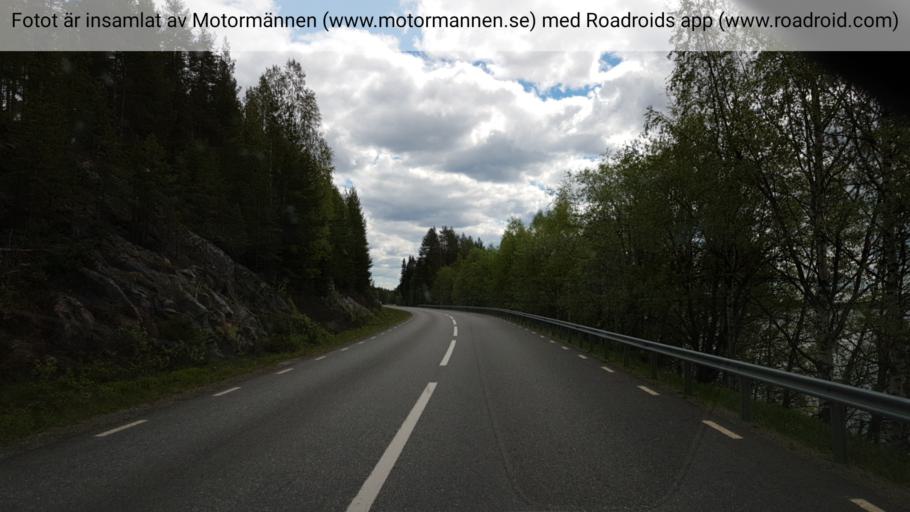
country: SE
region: Vaesterbotten
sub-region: Norsjo Kommun
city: Norsjoe
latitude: 64.8425
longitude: 19.7564
